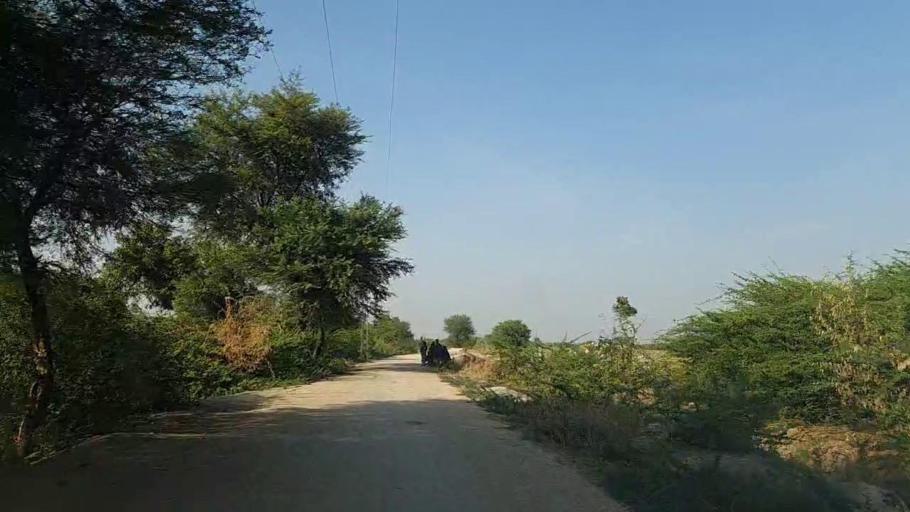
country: PK
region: Sindh
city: Naukot
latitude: 24.9365
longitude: 69.4590
